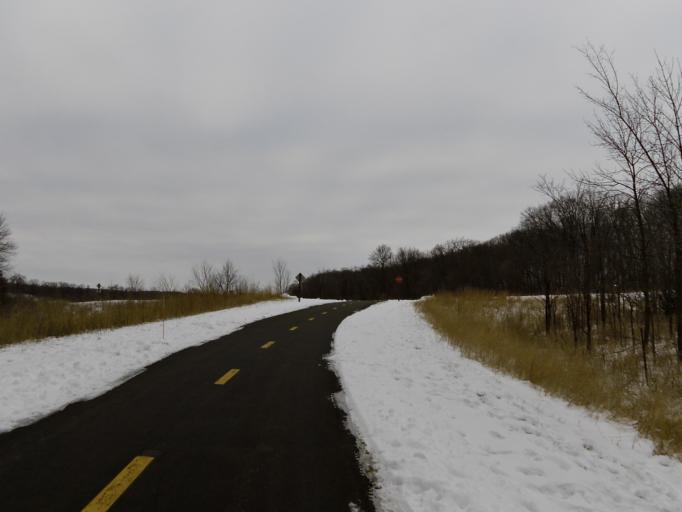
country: US
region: Minnesota
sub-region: Scott County
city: Prior Lake
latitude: 44.7133
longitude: -93.4690
